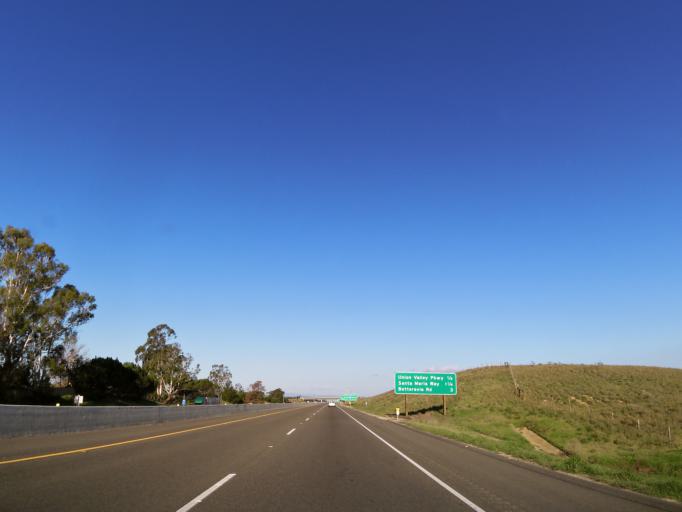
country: US
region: California
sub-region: Santa Barbara County
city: Orcutt
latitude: 34.8737
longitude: -120.4032
